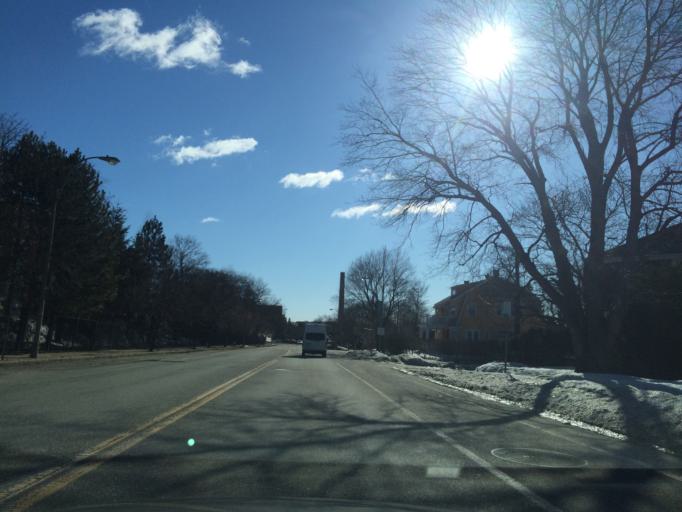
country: US
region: Massachusetts
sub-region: Middlesex County
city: Watertown
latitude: 42.3627
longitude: -71.1703
